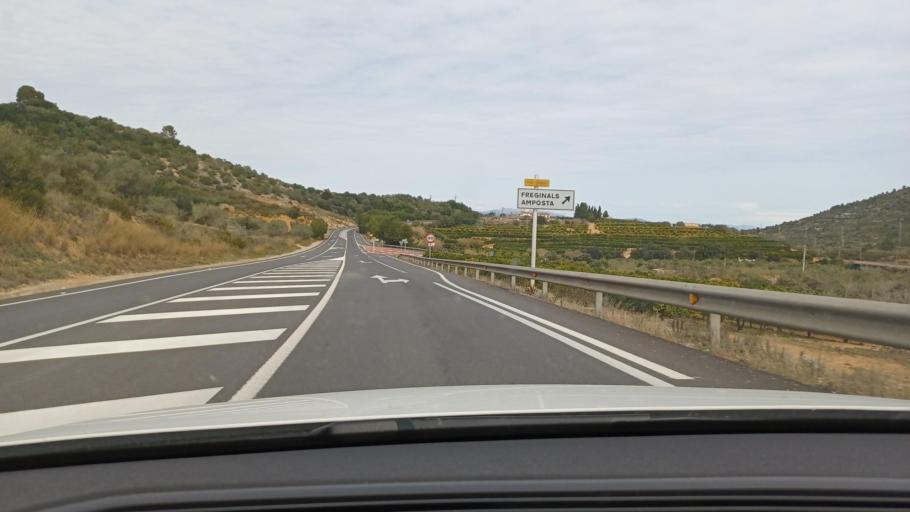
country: ES
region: Catalonia
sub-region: Provincia de Tarragona
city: Santa Barbara
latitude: 40.6743
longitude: 0.5098
